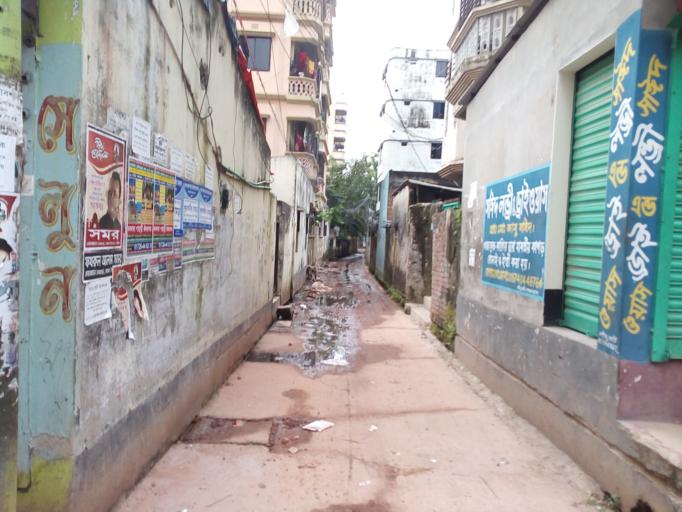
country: BD
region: Dhaka
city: Tungi
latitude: 23.8449
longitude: 90.2538
